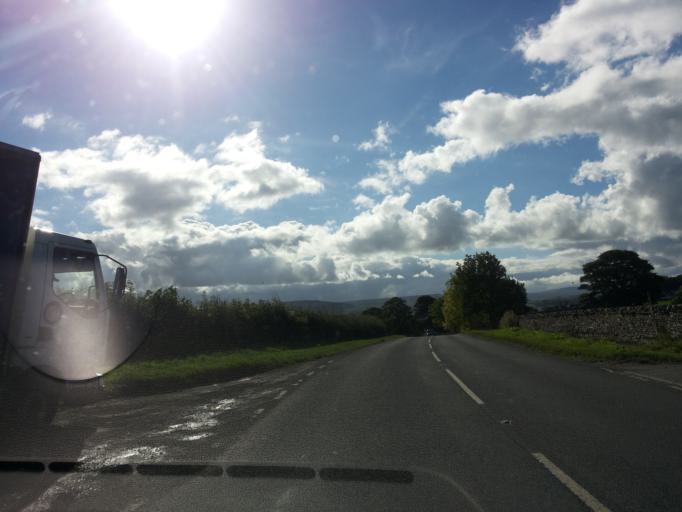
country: GB
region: England
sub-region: North Yorkshire
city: Leyburn
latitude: 54.3182
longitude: -1.8228
